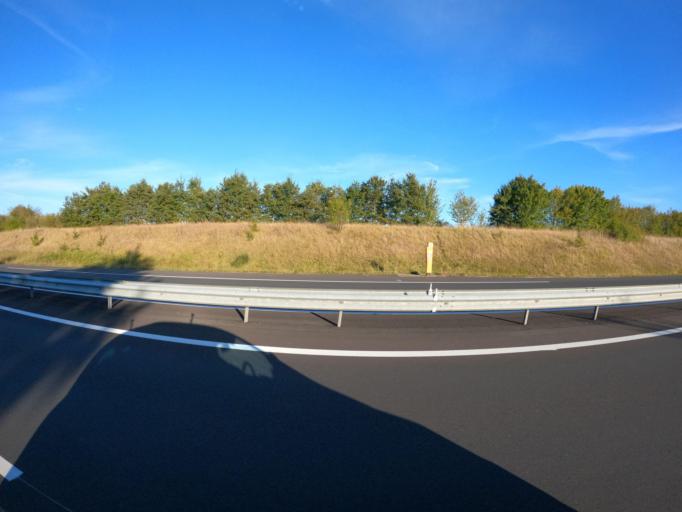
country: FR
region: Pays de la Loire
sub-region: Departement de la Vendee
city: Mortagne-sur-Sevre
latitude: 46.9846
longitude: -0.9177
